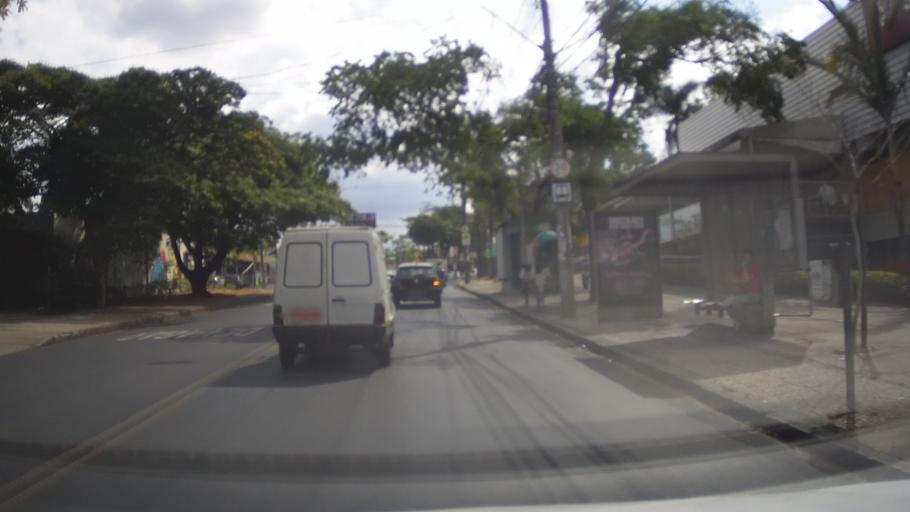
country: BR
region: Minas Gerais
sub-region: Belo Horizonte
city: Belo Horizonte
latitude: -19.8460
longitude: -43.9733
